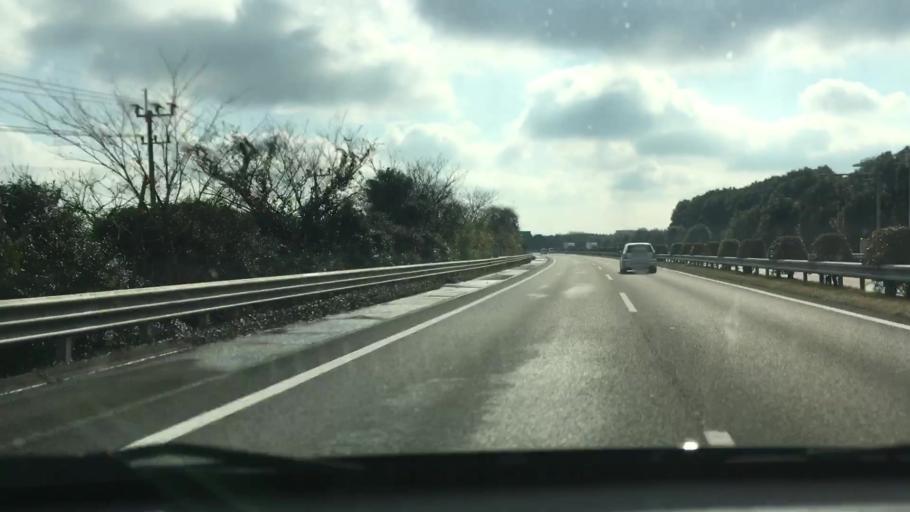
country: JP
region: Kumamoto
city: Kumamoto
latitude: 32.8002
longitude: 130.7912
